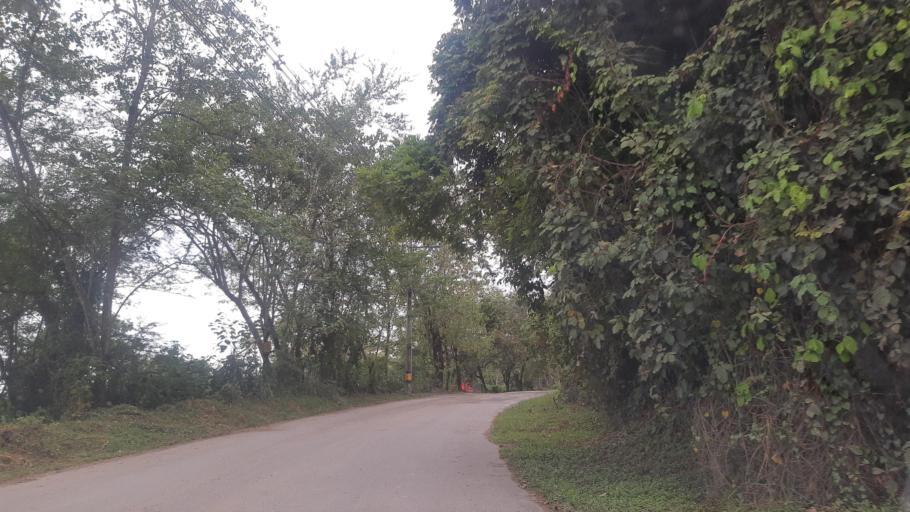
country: CO
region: Antioquia
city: Puerto Triunfo
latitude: 5.8771
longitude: -74.6358
